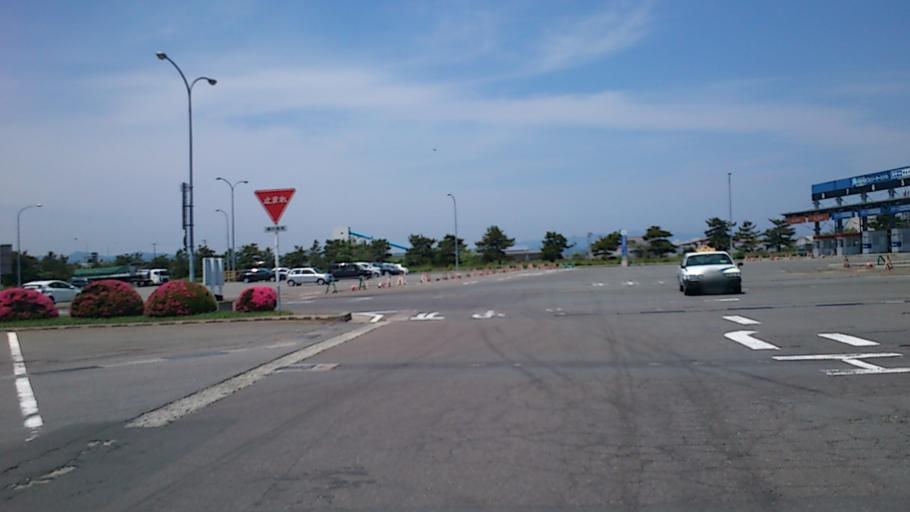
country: JP
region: Aomori
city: Aomori Shi
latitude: 40.8446
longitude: 140.7157
